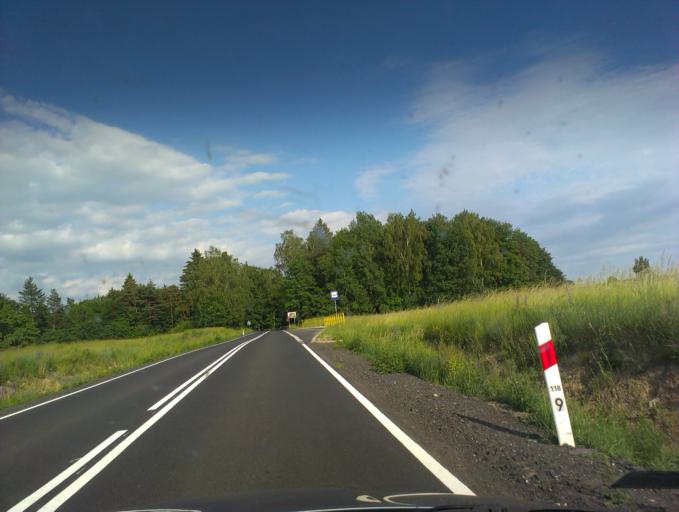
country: PL
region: West Pomeranian Voivodeship
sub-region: Powiat szczecinecki
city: Borne Sulinowo
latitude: 53.6211
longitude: 16.5302
